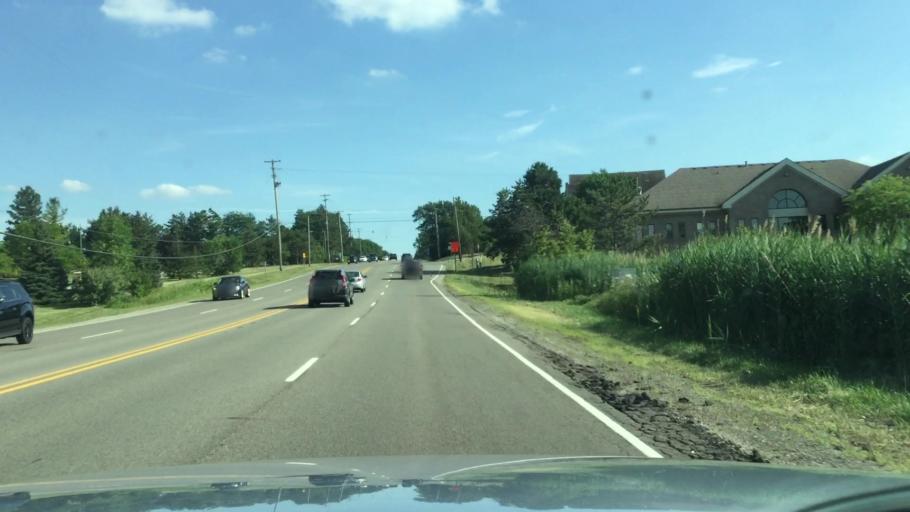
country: US
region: Michigan
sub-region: Genesee County
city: Grand Blanc
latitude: 42.9032
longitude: -83.6028
